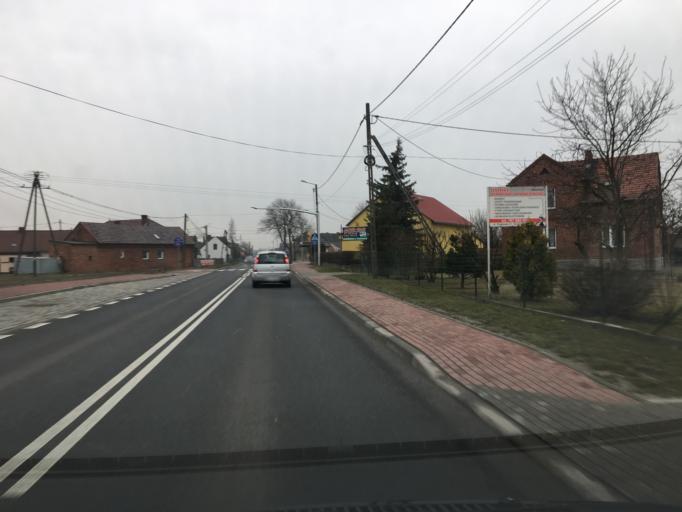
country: PL
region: Opole Voivodeship
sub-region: Powiat kedzierzynsko-kozielski
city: Kedzierzyn-Kozle
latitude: 50.3163
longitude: 18.2246
